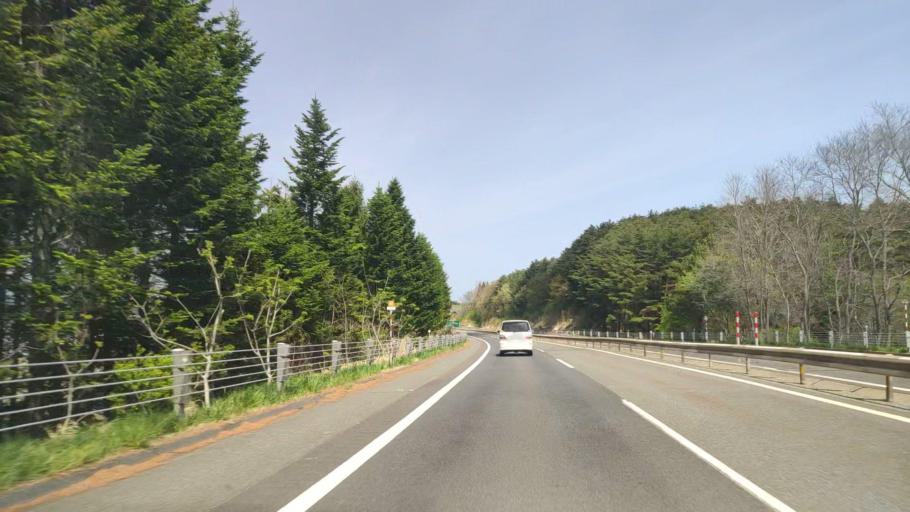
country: JP
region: Aomori
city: Hachinohe
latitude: 40.4705
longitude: 141.4614
